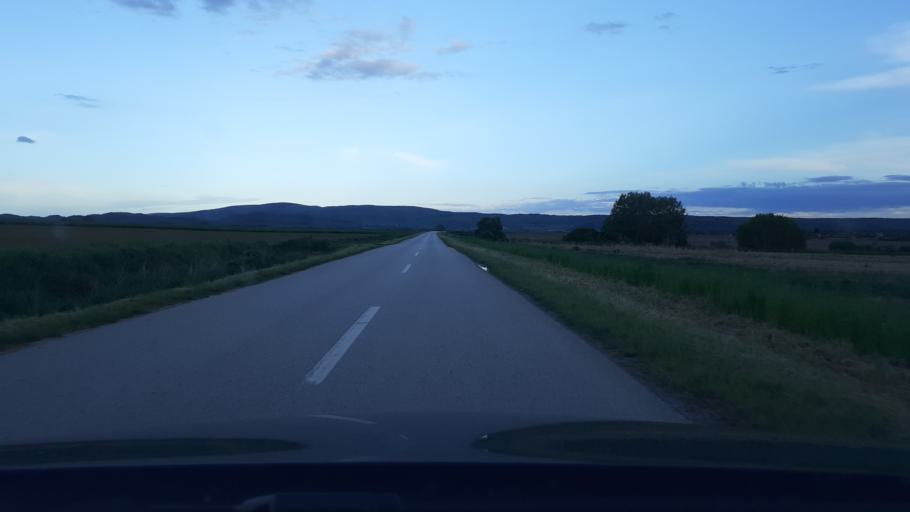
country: HR
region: Pozesko-Slavonska
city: Gradac
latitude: 45.3263
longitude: 17.8040
